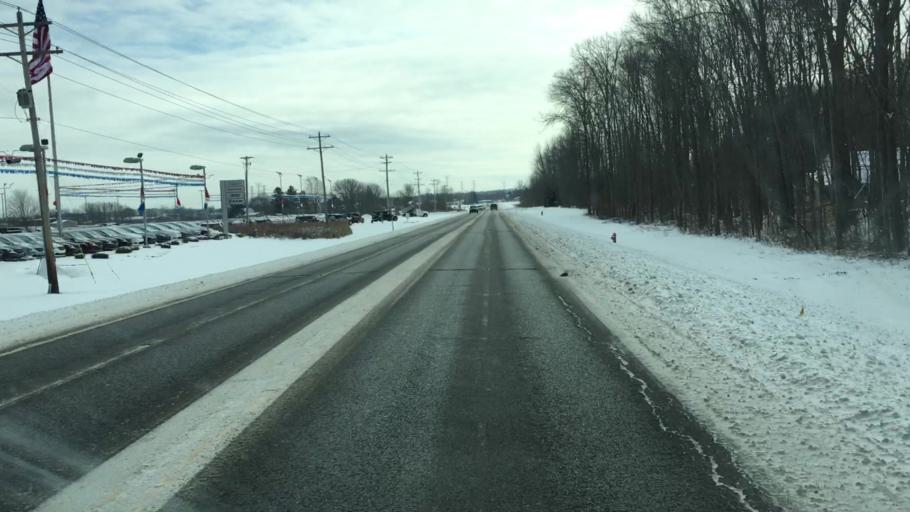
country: US
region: Ohio
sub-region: Columbiana County
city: Columbiana
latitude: 40.8960
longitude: -80.6804
